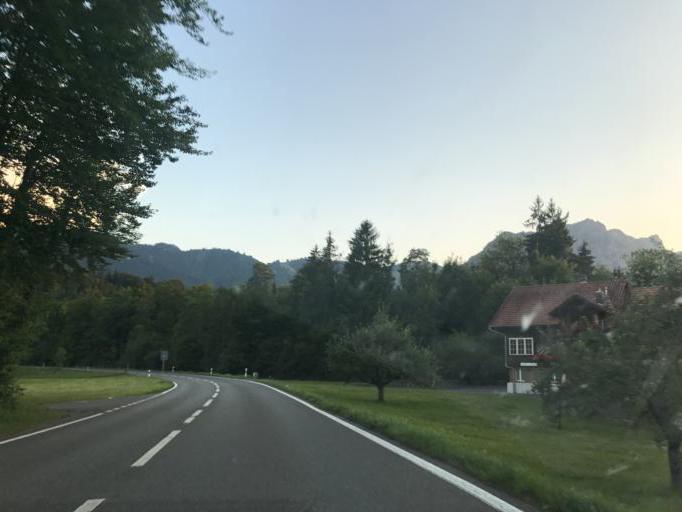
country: CH
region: Bern
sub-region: Frutigen-Niedersimmental District
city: Wimmis
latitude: 46.7104
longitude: 7.6310
